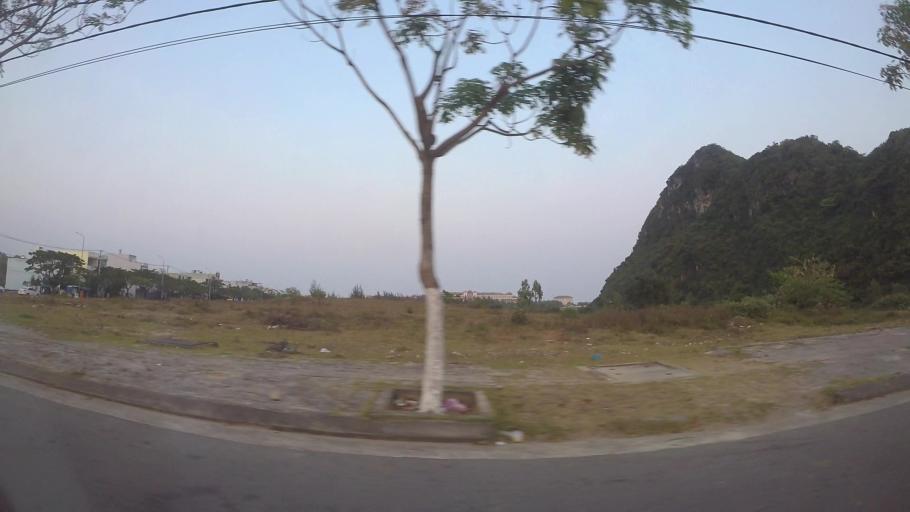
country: VN
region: Da Nang
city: Ngu Hanh Son
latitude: 16.0057
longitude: 108.2595
